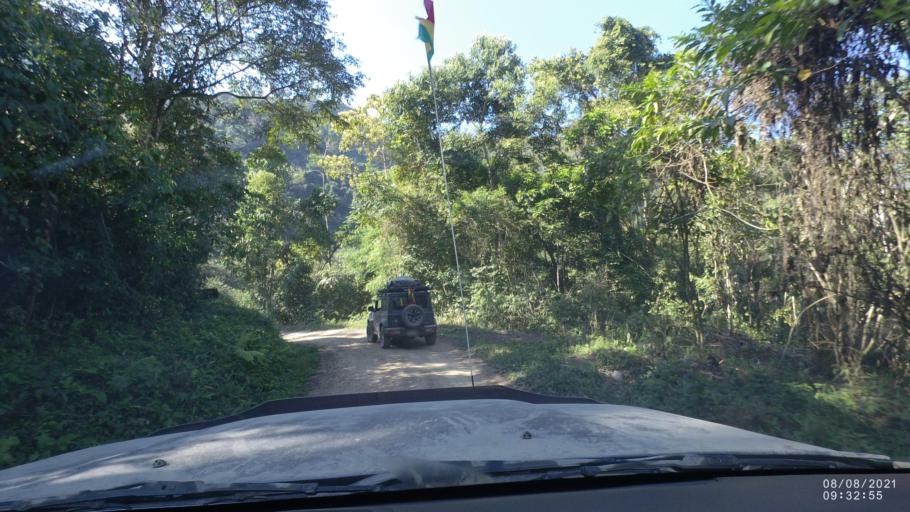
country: BO
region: La Paz
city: Quime
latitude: -16.5889
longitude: -66.7031
